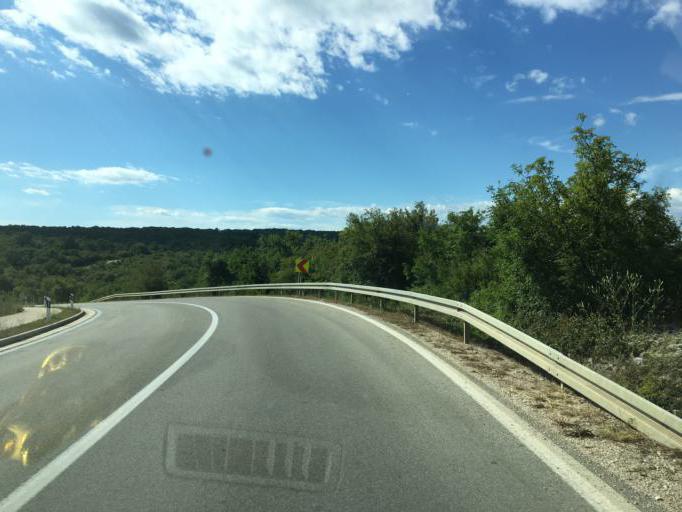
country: HR
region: Primorsko-Goranska
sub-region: Grad Krk
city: Krk
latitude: 45.0523
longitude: 14.5625
